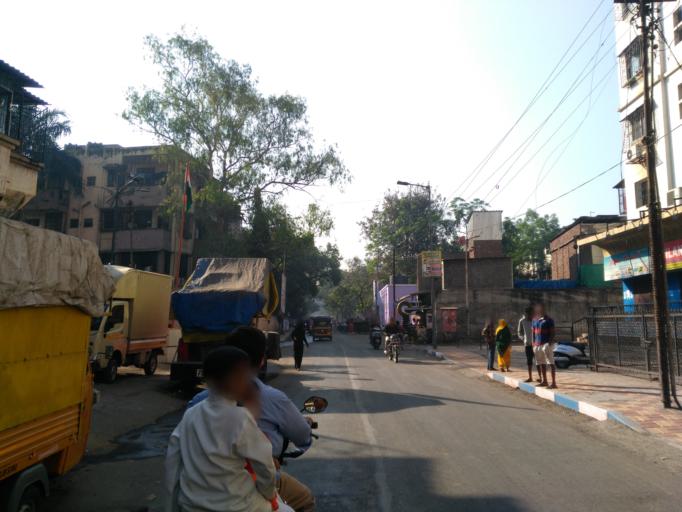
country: IN
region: Maharashtra
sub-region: Pune Division
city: Pune
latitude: 18.5141
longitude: 73.8712
